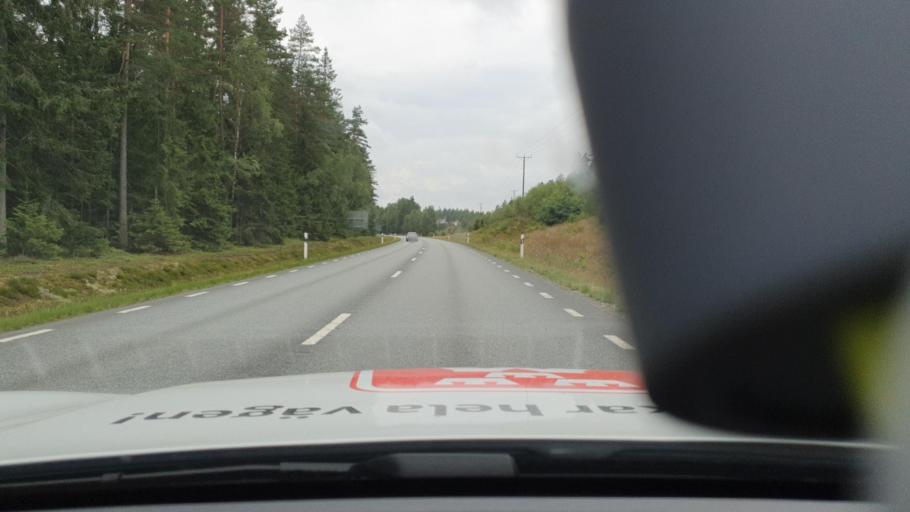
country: SE
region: Joenkoeping
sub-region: Gislaveds Kommun
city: Gislaved
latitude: 57.4223
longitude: 13.6059
